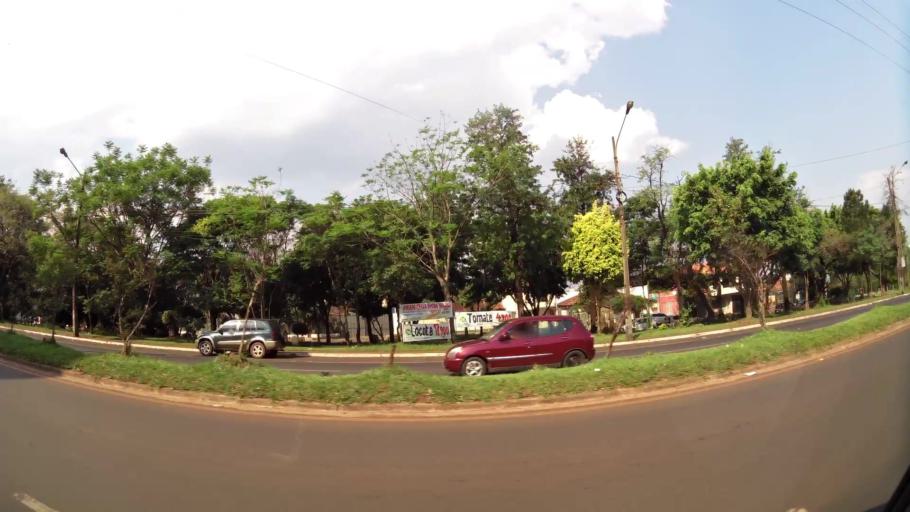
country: PY
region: Alto Parana
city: Presidente Franco
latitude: -25.5230
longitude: -54.6389
